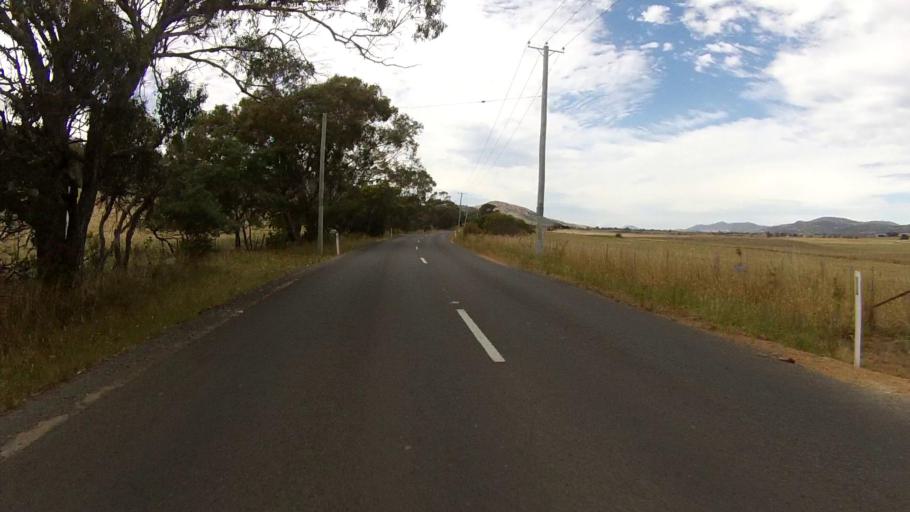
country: AU
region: Tasmania
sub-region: Clarence
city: Cambridge
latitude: -42.7216
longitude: 147.3934
